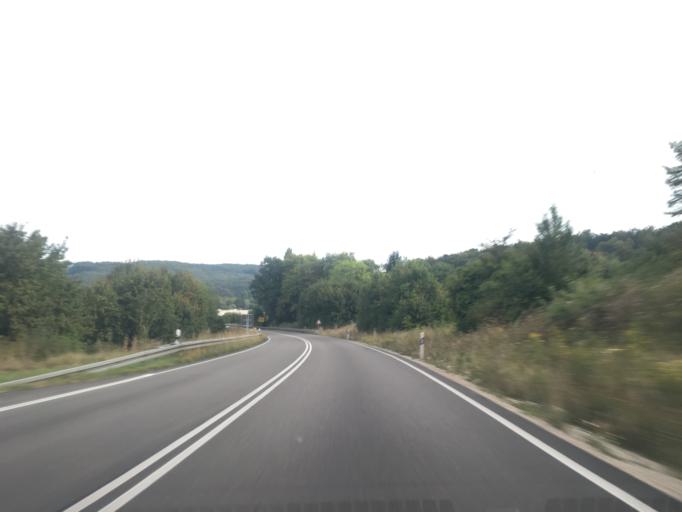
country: DE
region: Baden-Wuerttemberg
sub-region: Regierungsbezirk Stuttgart
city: Neckartailfingen
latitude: 48.6092
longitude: 9.2545
